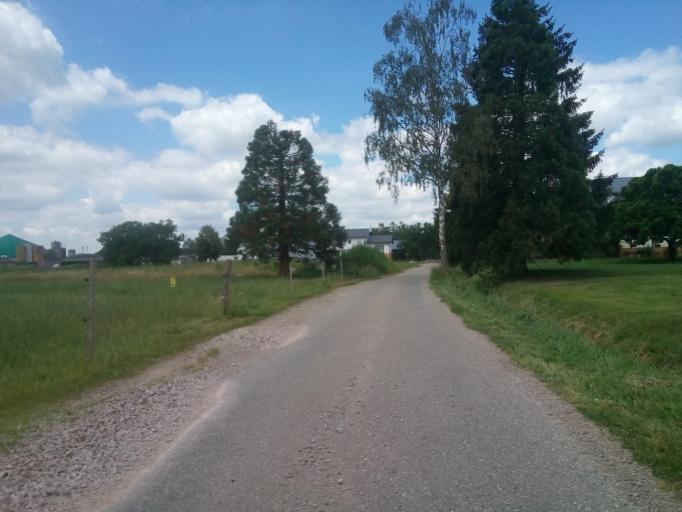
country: DE
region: Baden-Wuerttemberg
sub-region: Freiburg Region
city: Renchen
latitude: 48.6211
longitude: 7.9757
